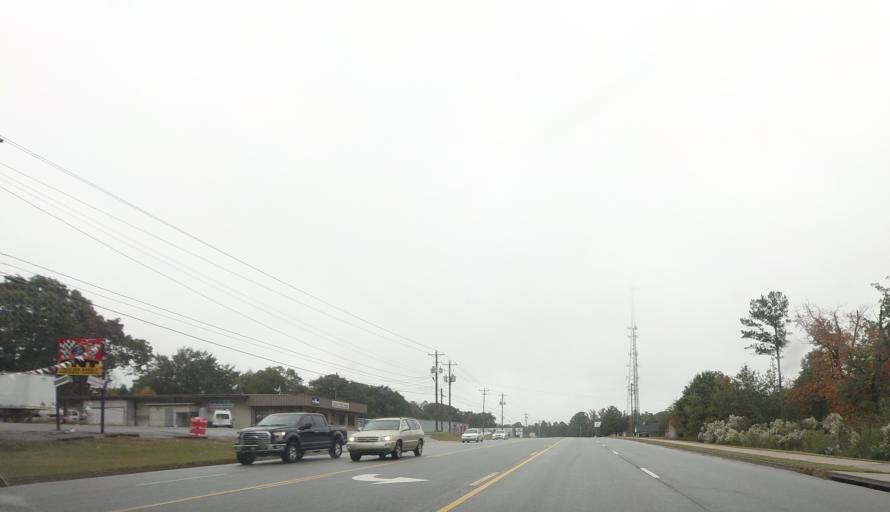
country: US
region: Georgia
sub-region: Houston County
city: Centerville
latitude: 32.6045
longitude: -83.6650
